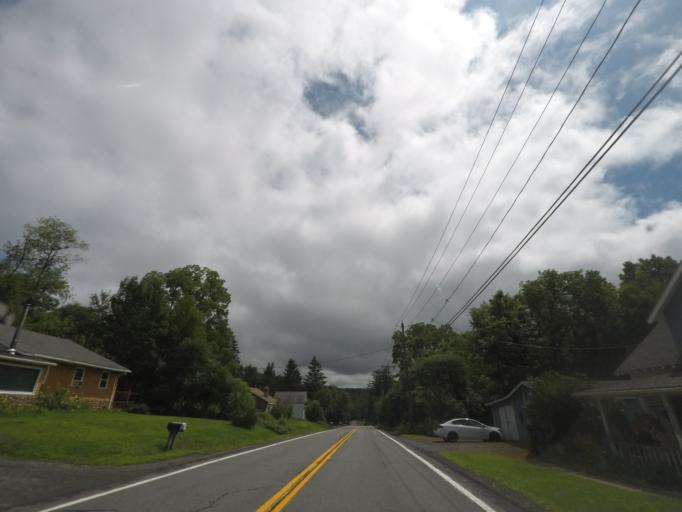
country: US
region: New York
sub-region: Rensselaer County
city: Averill Park
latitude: 42.5969
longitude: -73.5123
